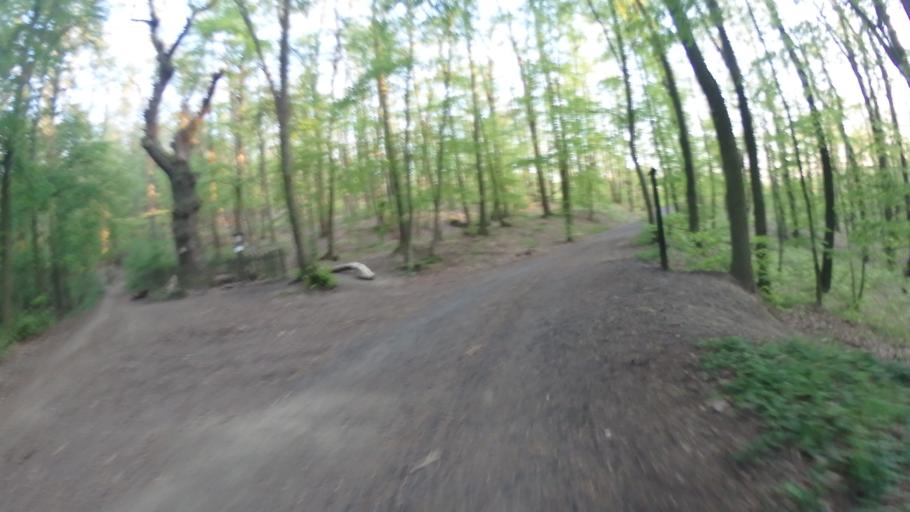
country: CZ
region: South Moravian
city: Troubsko
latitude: 49.1932
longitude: 16.5151
